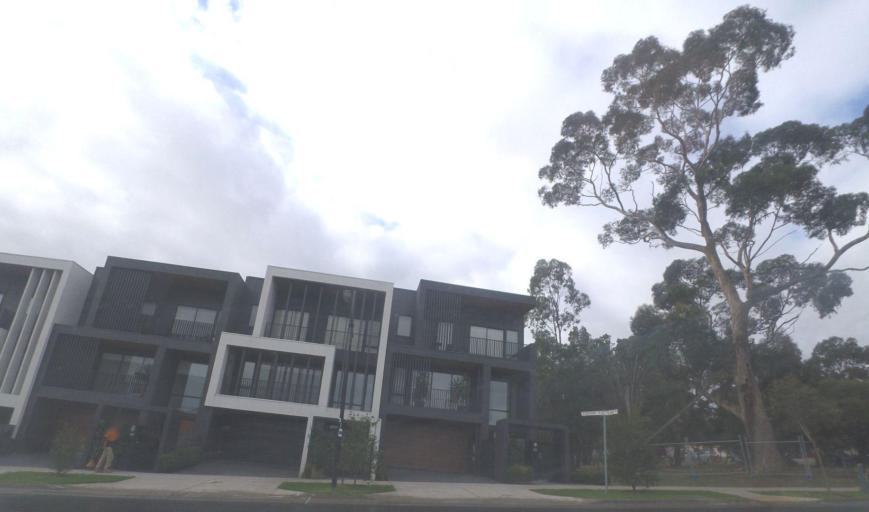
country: AU
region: Victoria
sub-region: Manningham
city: Doncaster
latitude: -37.7826
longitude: 145.1154
